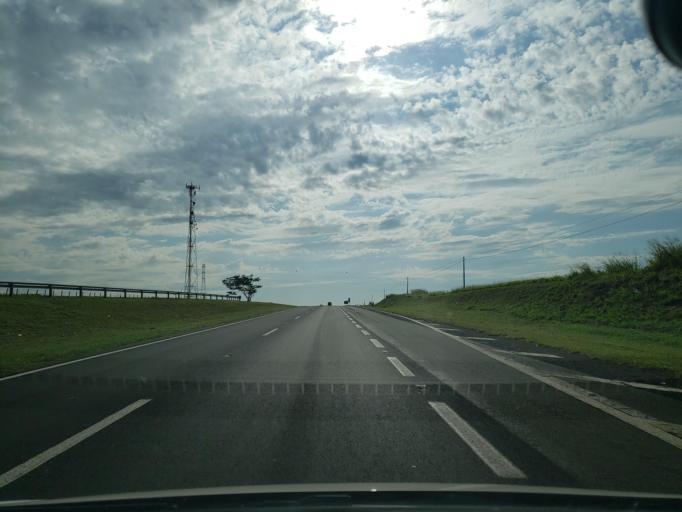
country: BR
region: Sao Paulo
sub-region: Birigui
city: Birigui
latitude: -21.3401
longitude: -50.3242
